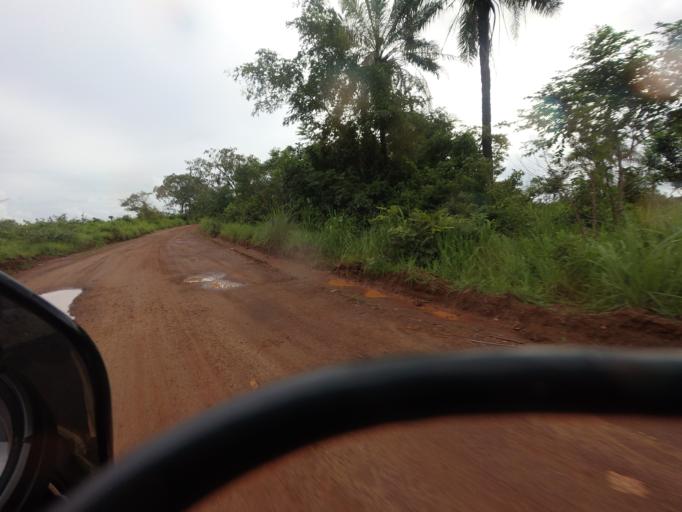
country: SL
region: Northern Province
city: Kambia
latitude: 9.1981
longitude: -12.8609
